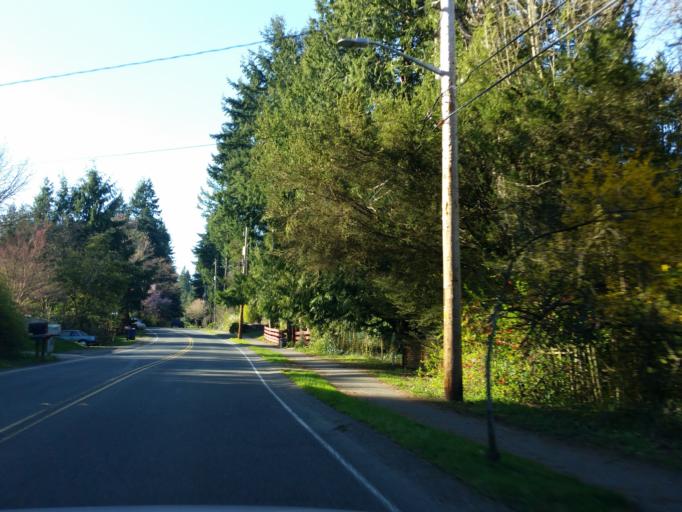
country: US
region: Washington
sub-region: King County
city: Lake Forest Park
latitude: 47.7534
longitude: -122.2832
